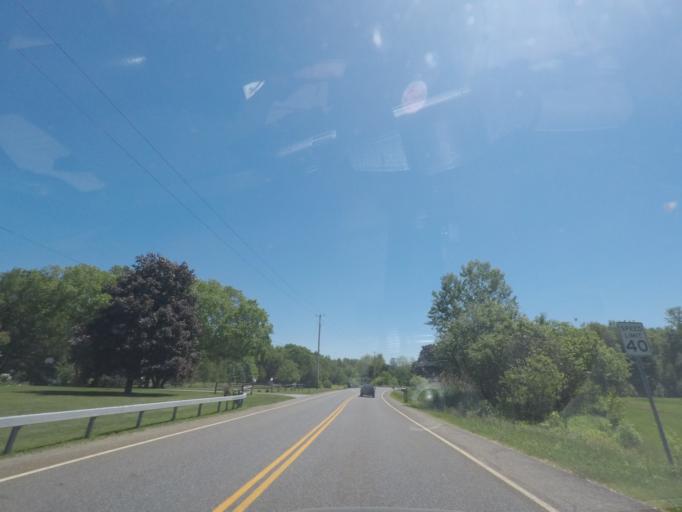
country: US
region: New York
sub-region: Saratoga County
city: Mechanicville
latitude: 42.9466
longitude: -73.7164
